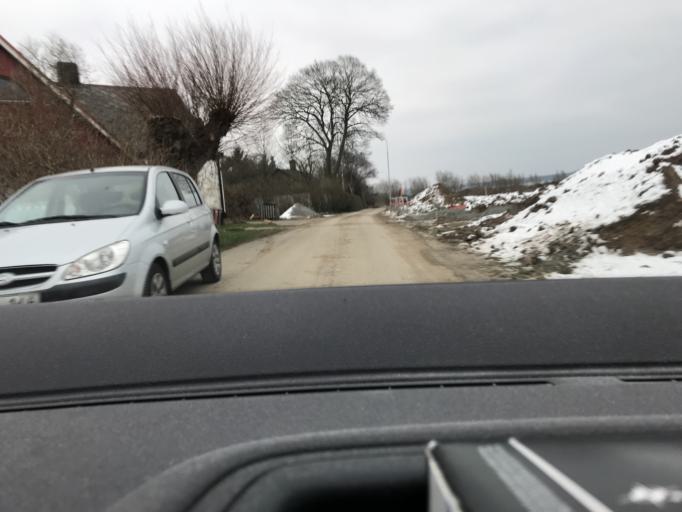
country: SE
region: Skane
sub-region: Ystads Kommun
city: Ystad
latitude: 55.4544
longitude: 13.8592
